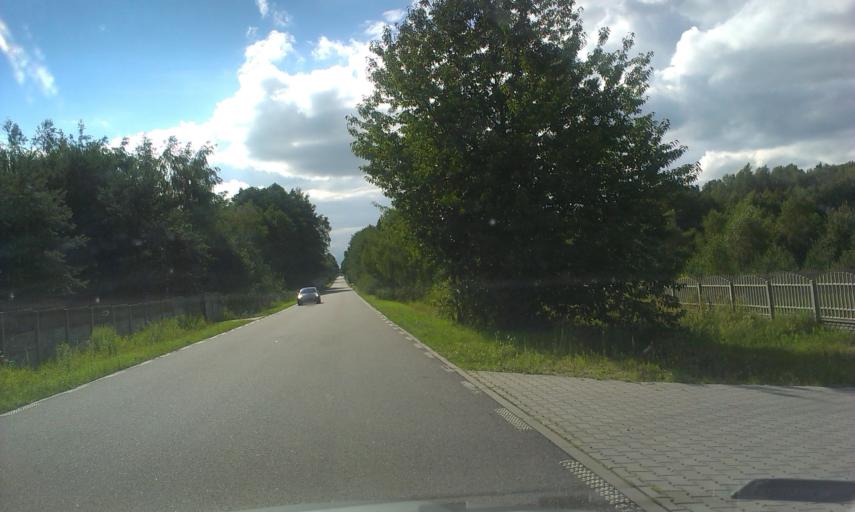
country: PL
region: Lodz Voivodeship
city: Zabia Wola
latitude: 51.9672
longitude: 20.6472
